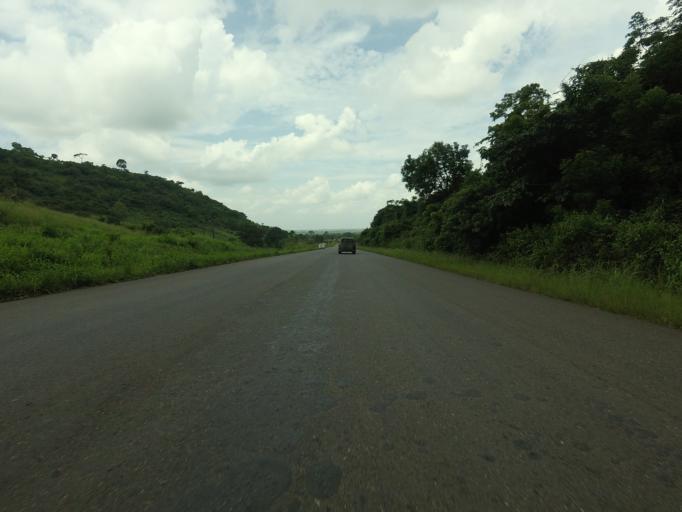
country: GH
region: Volta
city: Ho
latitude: 6.4253
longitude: 0.1694
